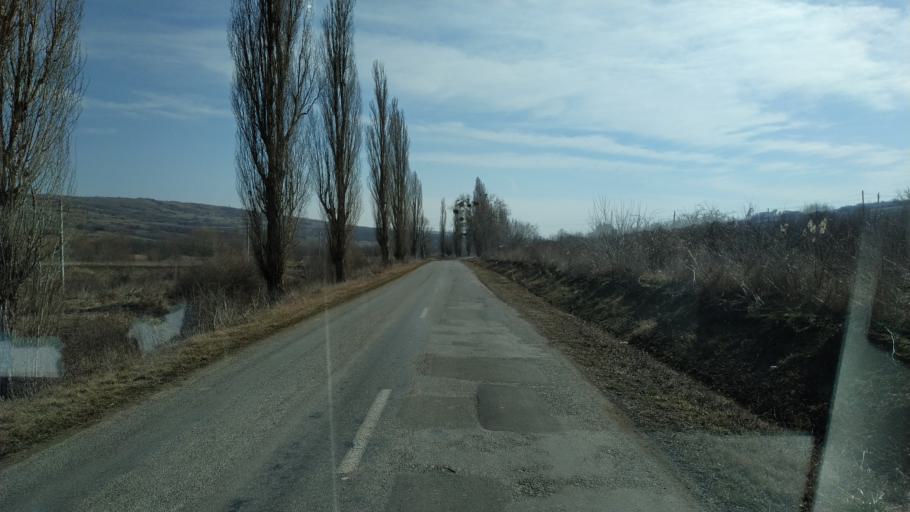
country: MD
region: Nisporeni
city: Nisporeni
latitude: 47.1629
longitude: 28.1020
